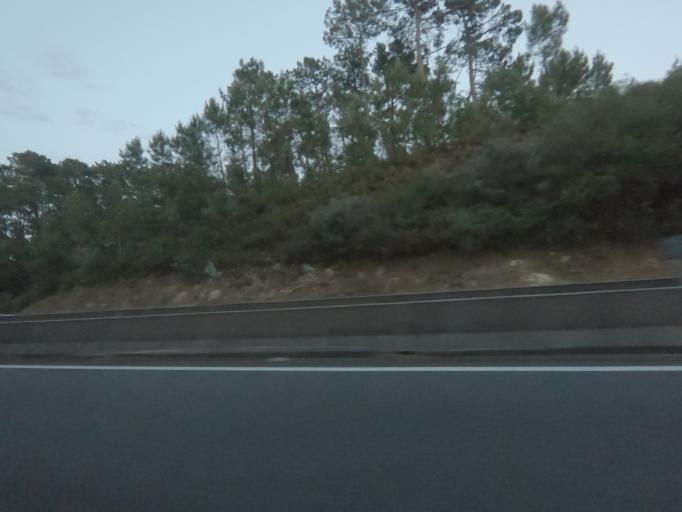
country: ES
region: Galicia
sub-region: Provincia de Pontevedra
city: Tui
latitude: 42.0791
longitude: -8.6323
